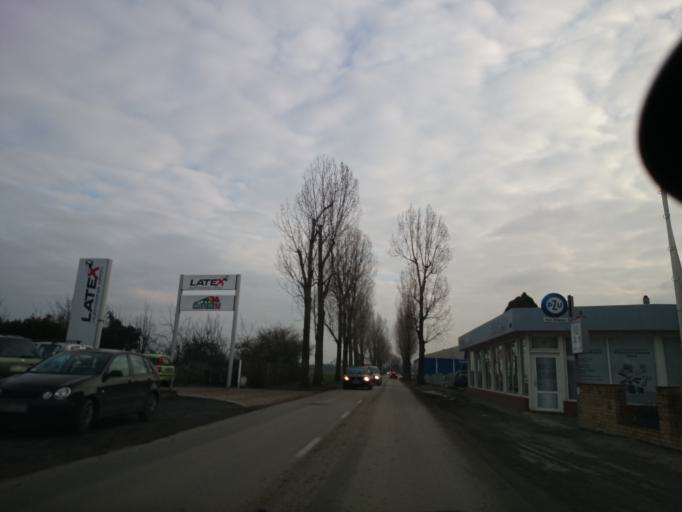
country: PL
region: Opole Voivodeship
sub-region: Powiat opolski
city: Opole
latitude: 50.6536
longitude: 17.9094
